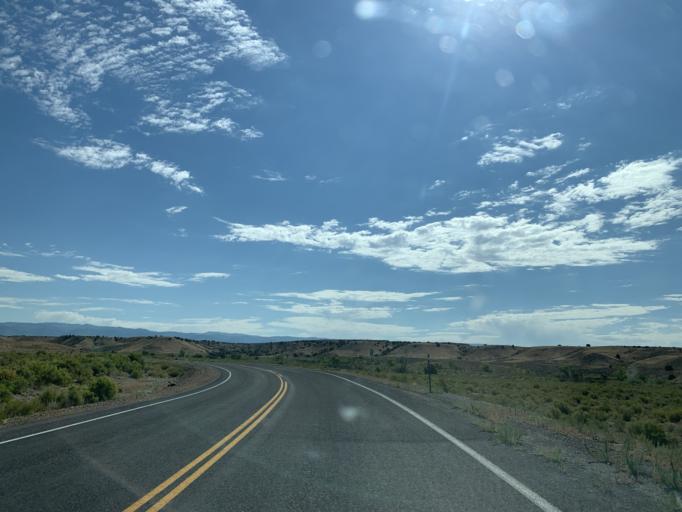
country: US
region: Utah
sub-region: Carbon County
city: Wellington
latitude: 39.5594
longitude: -110.6627
